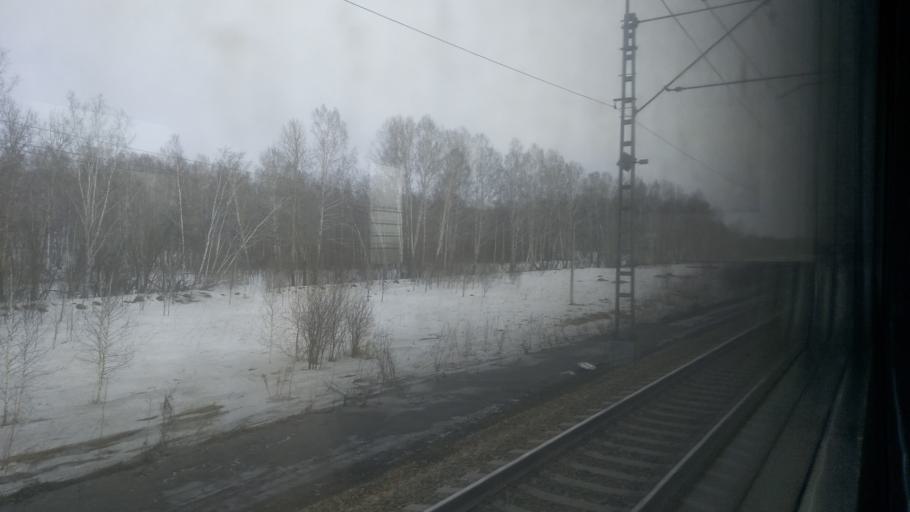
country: RU
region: Novosibirsk
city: Stantsionno-Oyashinskiy
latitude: 55.5062
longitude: 83.9240
